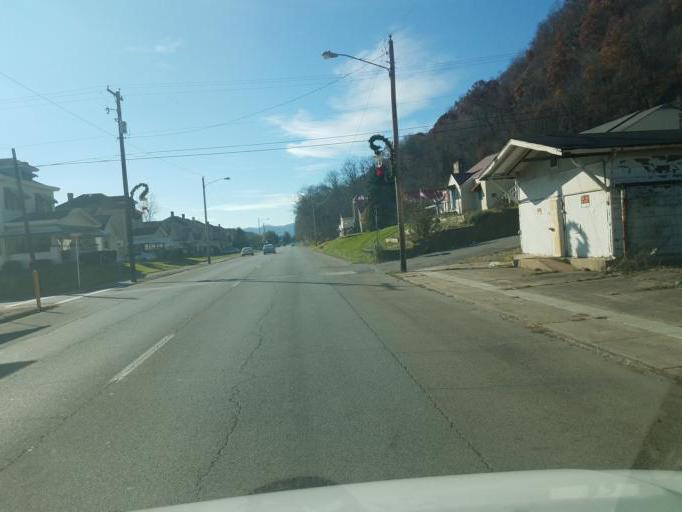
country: US
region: Ohio
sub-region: Scioto County
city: New Boston
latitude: 38.7473
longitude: -82.9464
